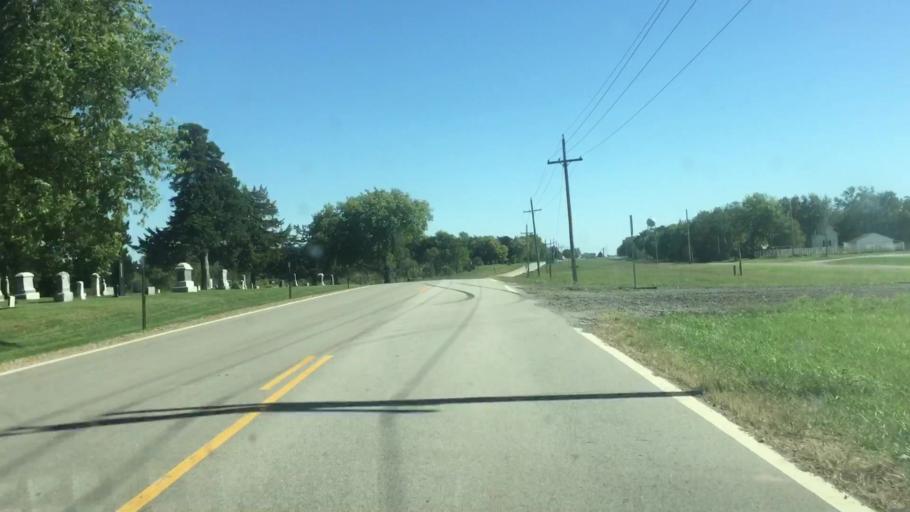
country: US
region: Kansas
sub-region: Jackson County
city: Holton
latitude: 39.6084
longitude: -95.7236
